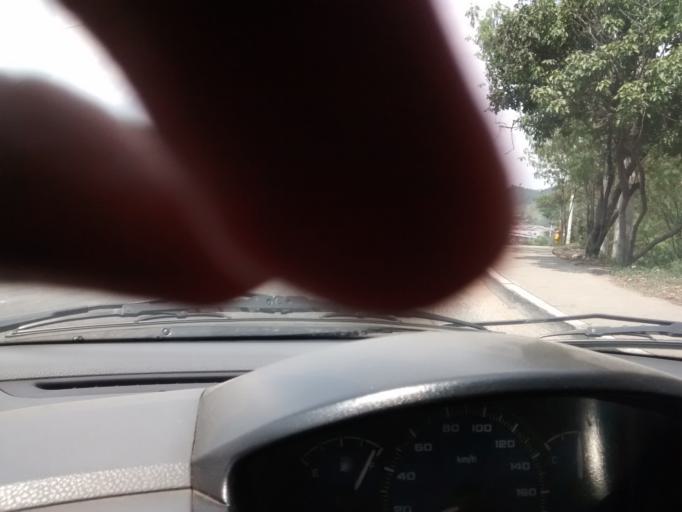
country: CO
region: Santander
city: Giron
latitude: 7.0818
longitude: -73.1696
